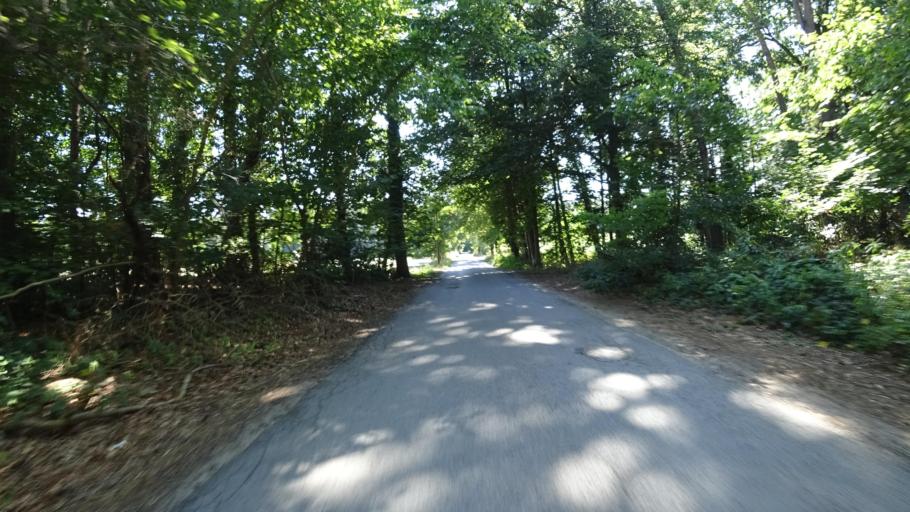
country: DE
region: North Rhine-Westphalia
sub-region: Regierungsbezirk Detmold
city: Steinhagen
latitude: 51.9458
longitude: 8.4608
